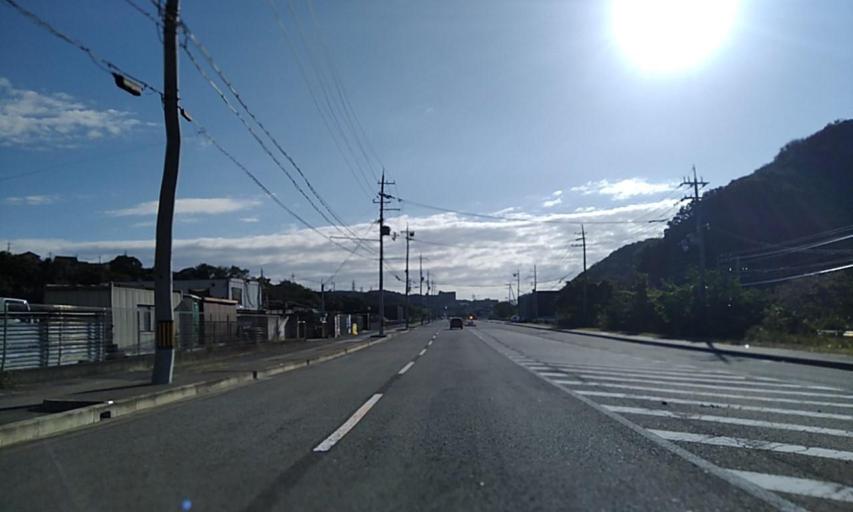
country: JP
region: Wakayama
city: Minato
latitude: 34.2698
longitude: 135.0859
